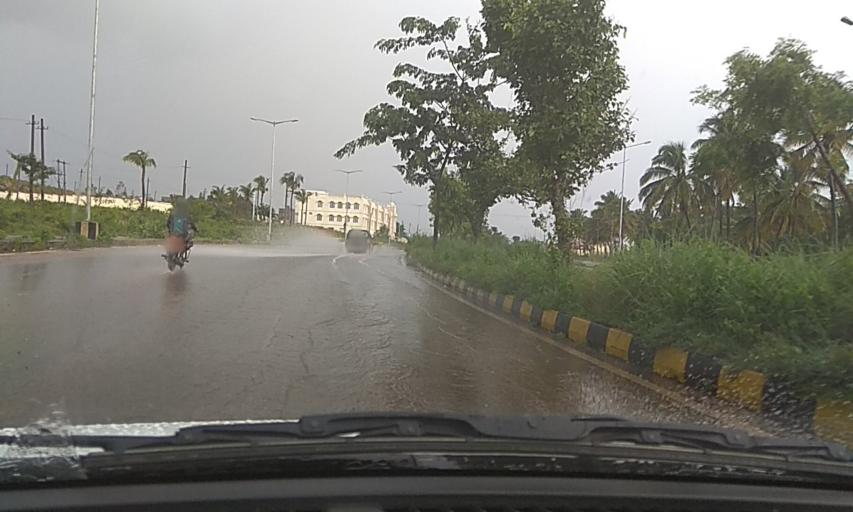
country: IN
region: Karnataka
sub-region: Mysore
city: Mysore
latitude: 12.3481
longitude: 76.6698
